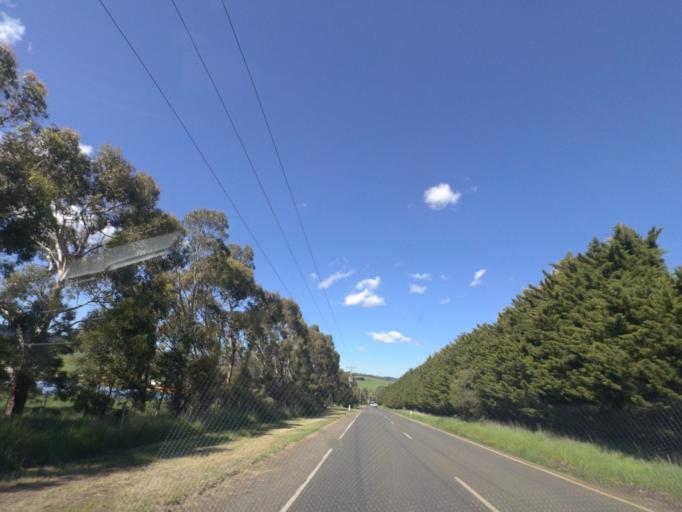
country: AU
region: Victoria
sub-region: Moorabool
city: Bacchus Marsh
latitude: -37.5648
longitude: 144.2612
